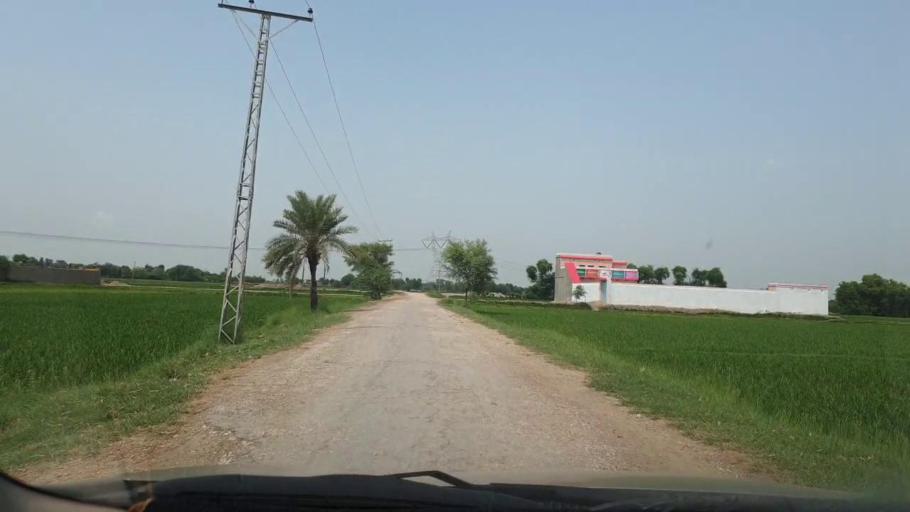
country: PK
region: Sindh
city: Larkana
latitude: 27.5779
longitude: 68.1427
